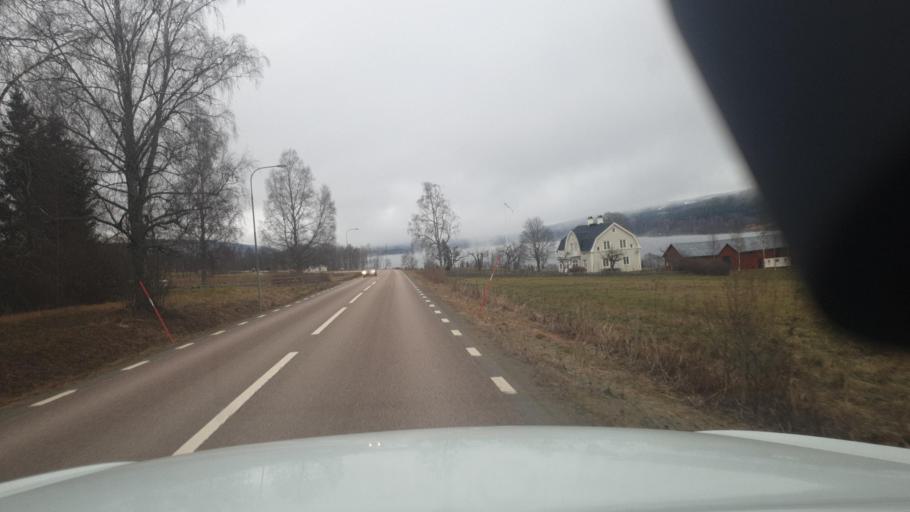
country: SE
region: Vaermland
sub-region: Sunne Kommun
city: Sunne
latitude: 59.8914
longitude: 12.9199
